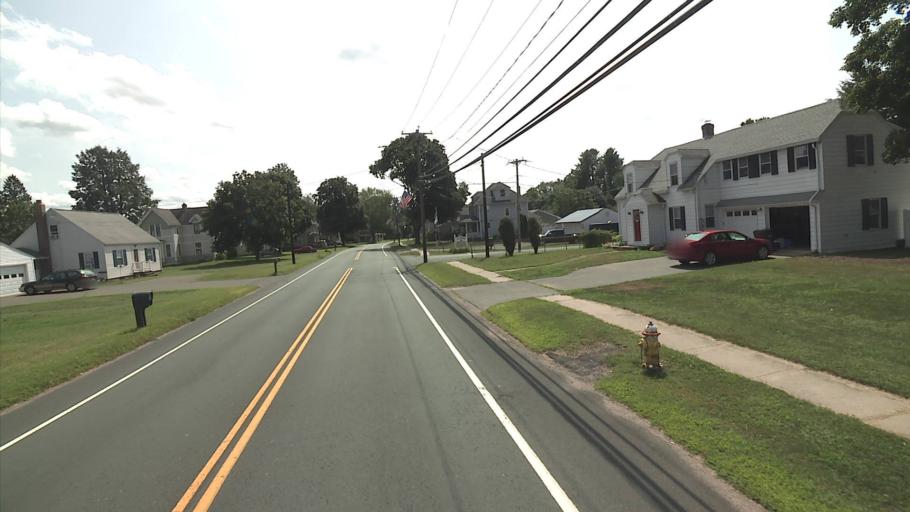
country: US
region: Connecticut
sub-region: Hartford County
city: Broad Brook
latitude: 41.9229
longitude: -72.5445
